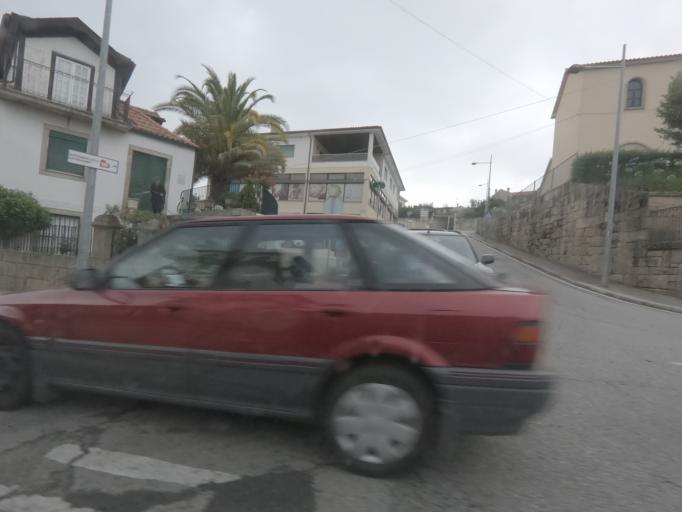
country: PT
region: Viseu
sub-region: Armamar
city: Armamar
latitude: 41.1067
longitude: -7.6924
